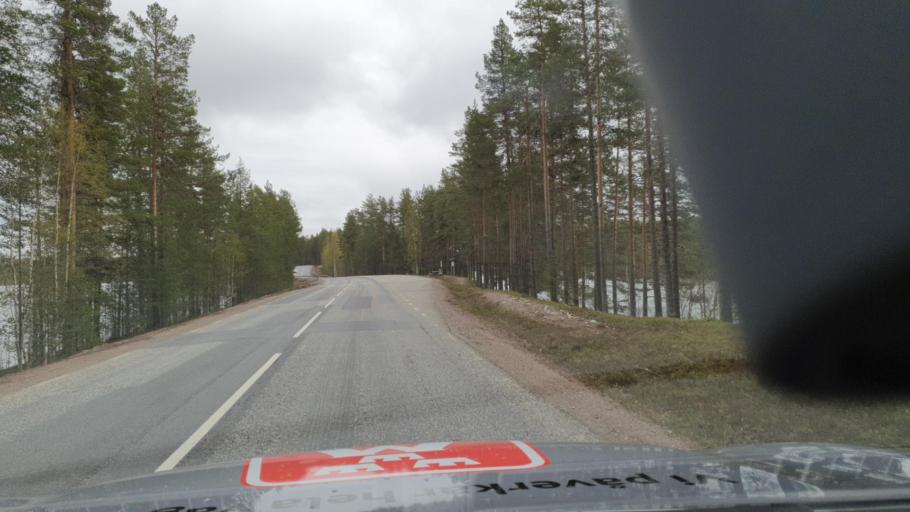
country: SE
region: Vaesternorrland
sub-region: Solleftea Kommun
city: Solleftea
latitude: 63.6486
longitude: 17.3754
